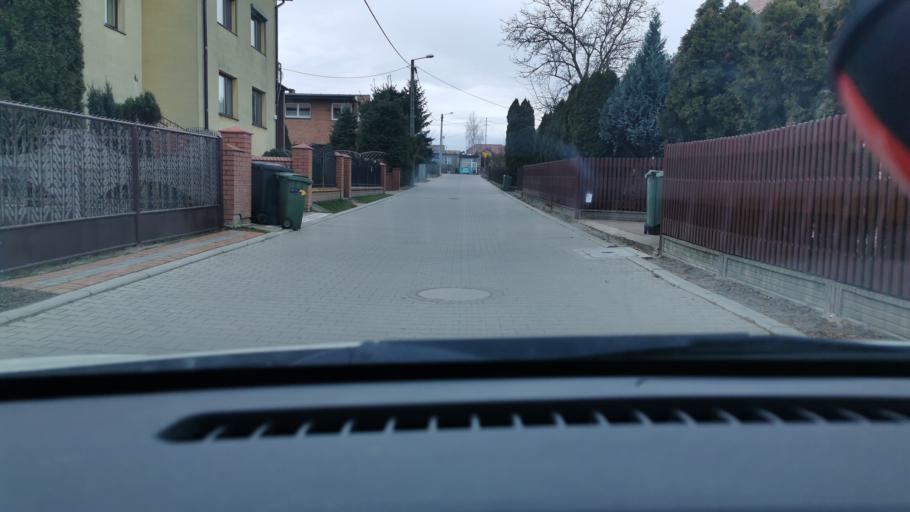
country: PL
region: Greater Poland Voivodeship
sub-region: Powiat ostrowski
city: Ostrow Wielkopolski
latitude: 51.6439
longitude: 17.8666
